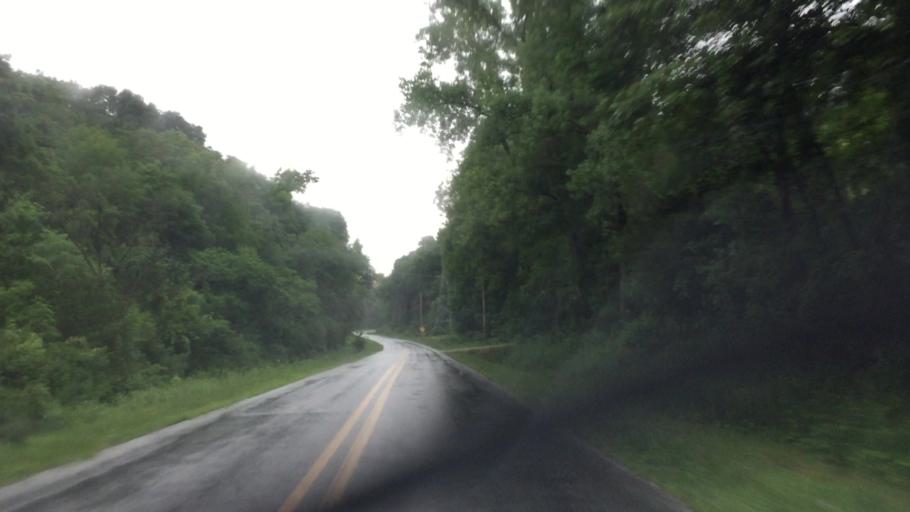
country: US
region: Iowa
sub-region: Lee County
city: Fort Madison
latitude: 40.6084
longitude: -91.2798
